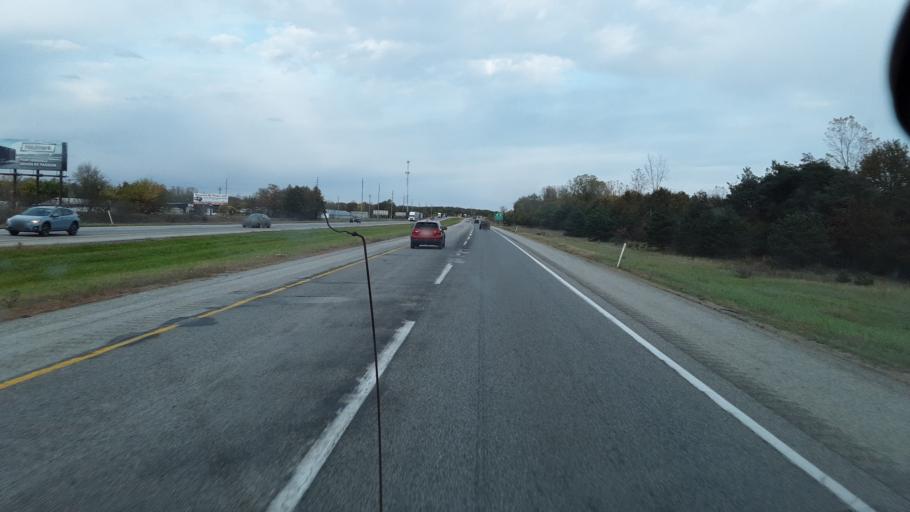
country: US
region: Indiana
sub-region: Elkhart County
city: Middlebury
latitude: 41.7383
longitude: -85.7367
